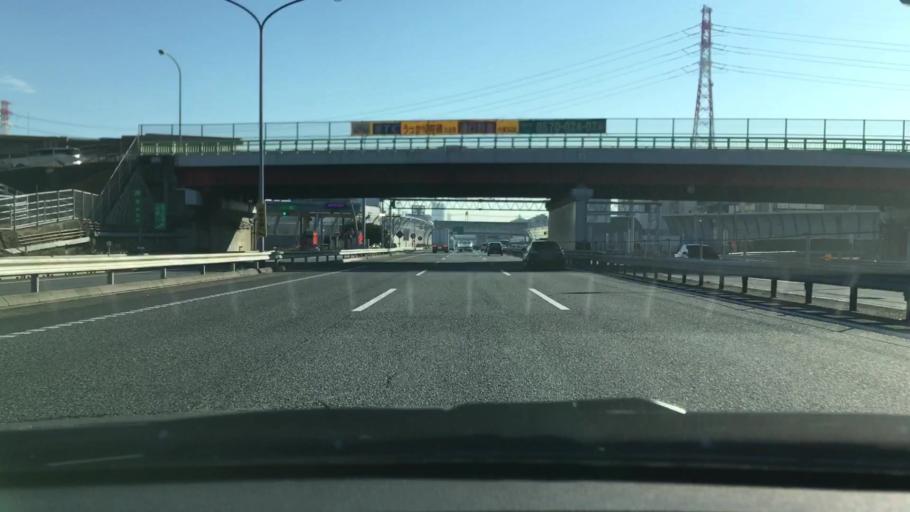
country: JP
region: Chiba
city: Funabashi
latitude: 35.7037
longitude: 139.9517
